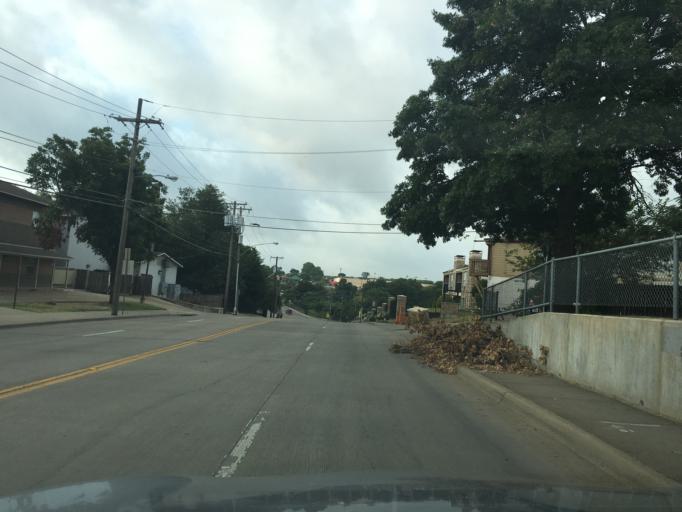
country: US
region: Texas
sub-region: Dallas County
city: University Park
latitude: 32.8658
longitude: -96.7501
